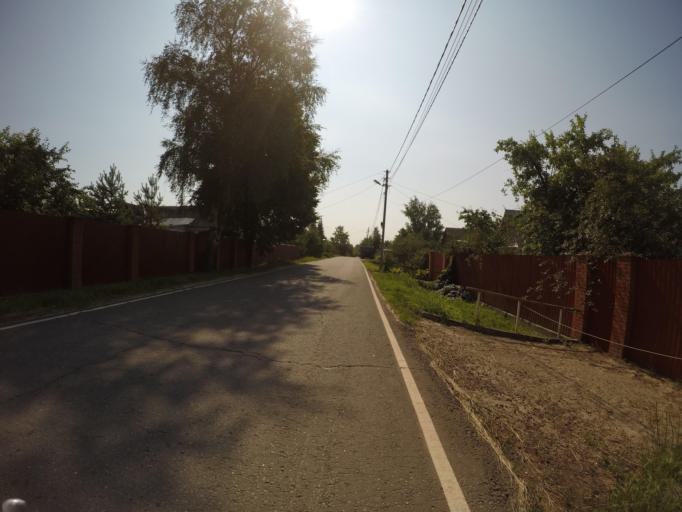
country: RU
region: Moskovskaya
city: Rechitsy
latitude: 55.6189
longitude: 38.5294
